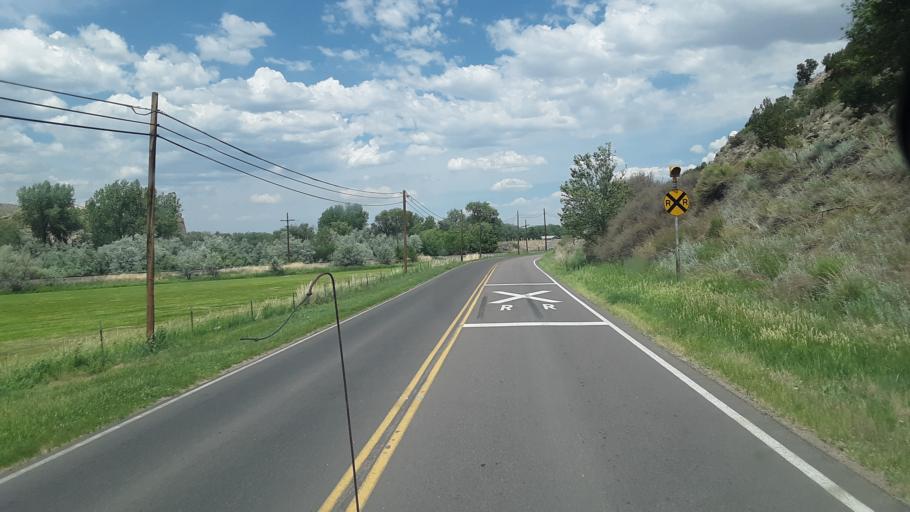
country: US
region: Colorado
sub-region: Fremont County
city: Florence
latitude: 38.4048
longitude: -105.1512
